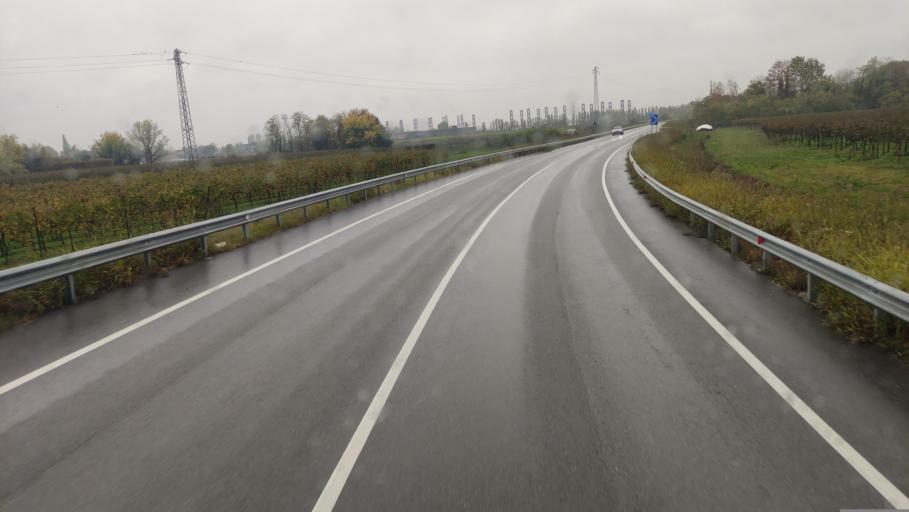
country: IT
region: Veneto
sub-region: Provincia di Treviso
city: Lancenigo-Villorba
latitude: 45.7426
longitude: 12.2660
